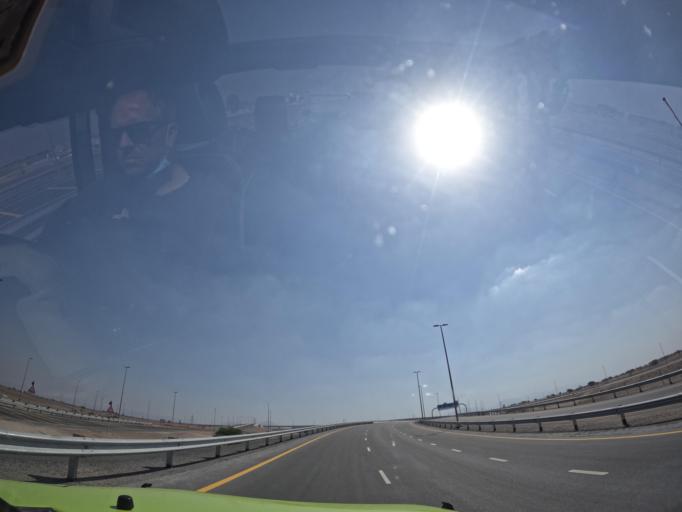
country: AE
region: Ash Shariqah
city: Adh Dhayd
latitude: 24.9113
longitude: 55.7955
